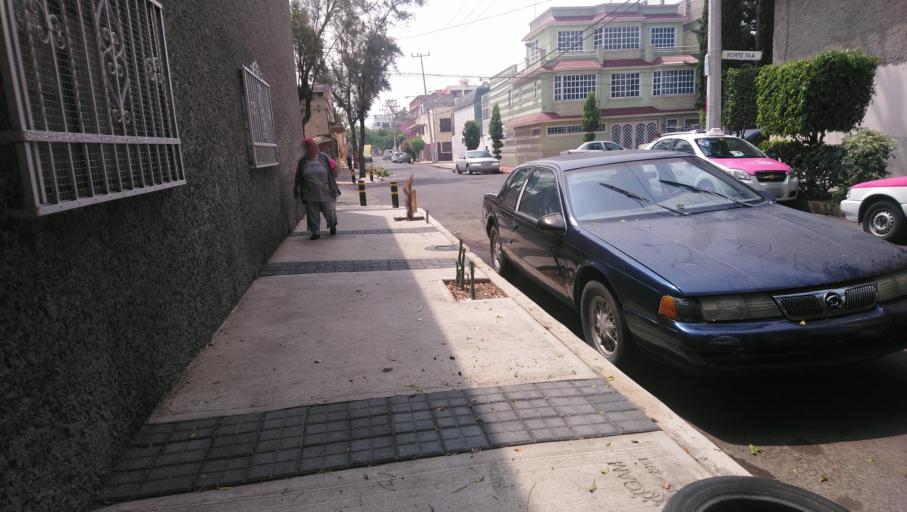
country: MX
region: Mexico City
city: Gustavo A. Madero
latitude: 19.4697
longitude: -99.1037
